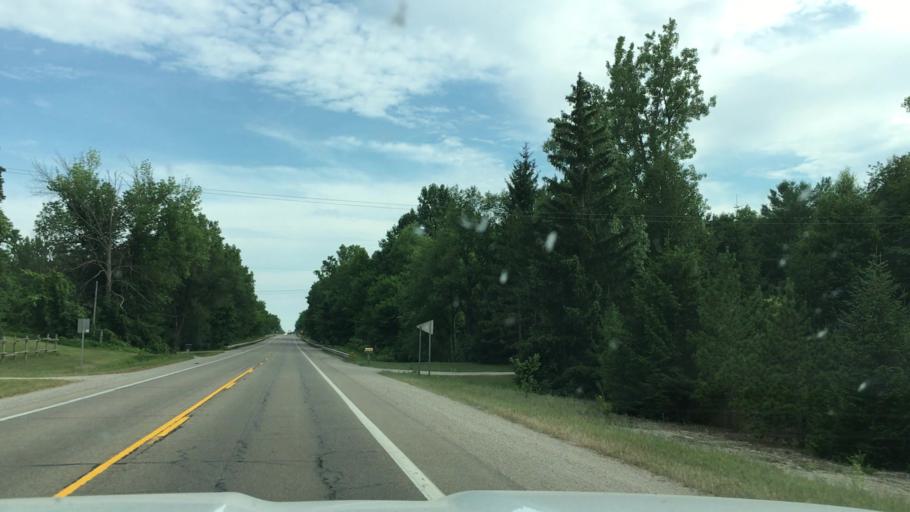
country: US
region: Michigan
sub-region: Lapeer County
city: Imlay City
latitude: 43.1333
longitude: -83.0736
